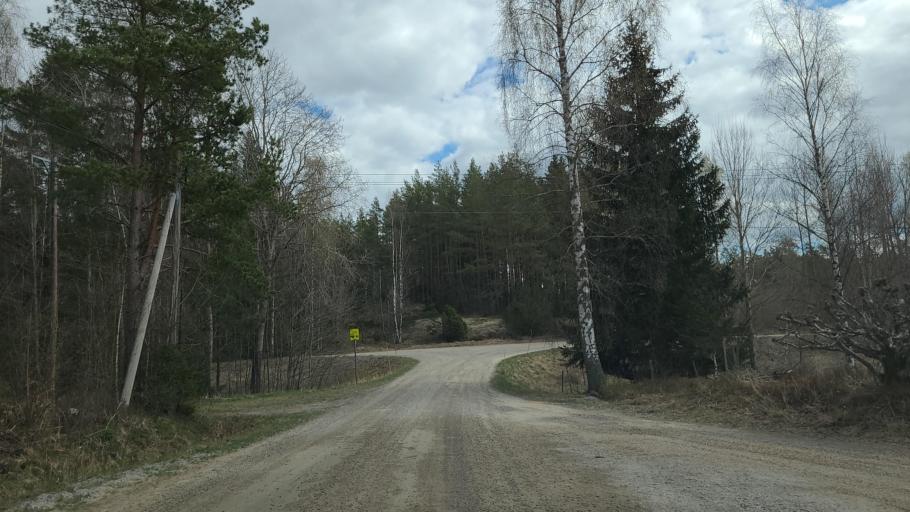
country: SE
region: OEstergoetland
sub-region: Norrkopings Kommun
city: Krokek
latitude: 58.6803
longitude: 16.4289
